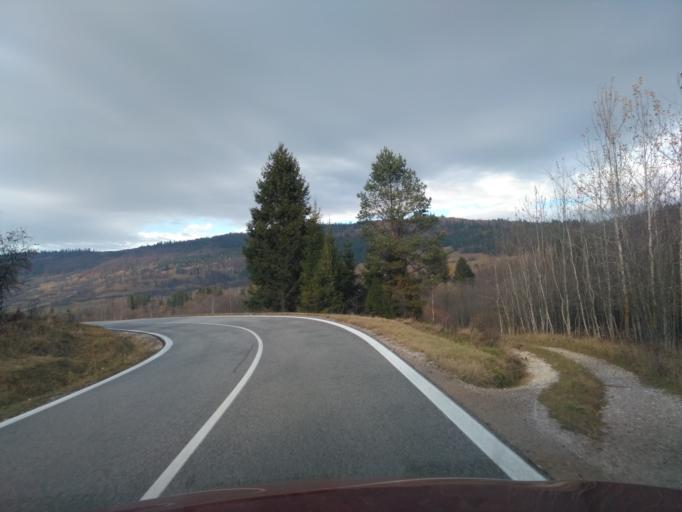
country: SK
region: Kosicky
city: Spisska Nova Ves
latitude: 48.8199
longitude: 20.6598
